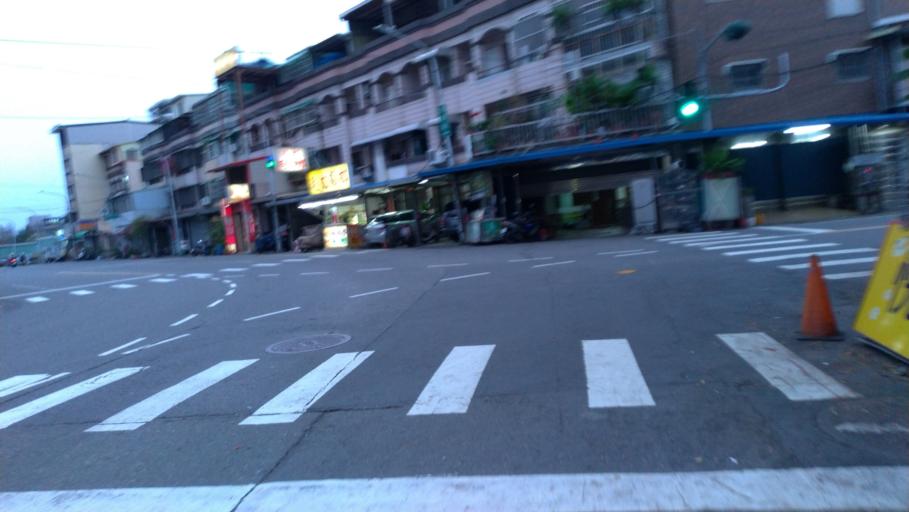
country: TW
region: Taiwan
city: Fengshan
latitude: 22.6542
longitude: 120.3630
